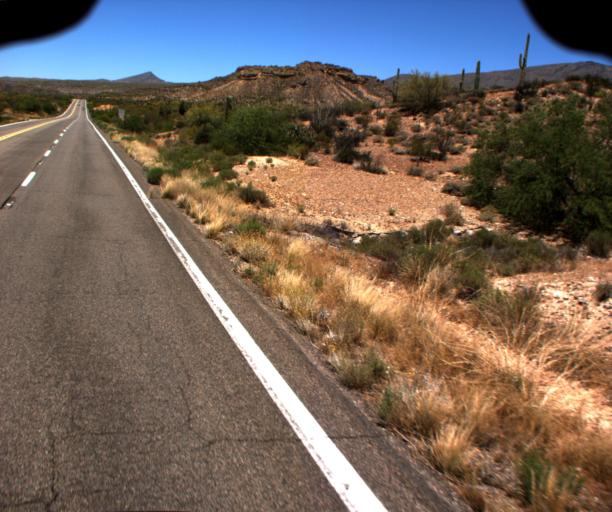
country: US
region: Arizona
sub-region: Pinal County
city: Kearny
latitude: 33.1354
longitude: -110.7860
